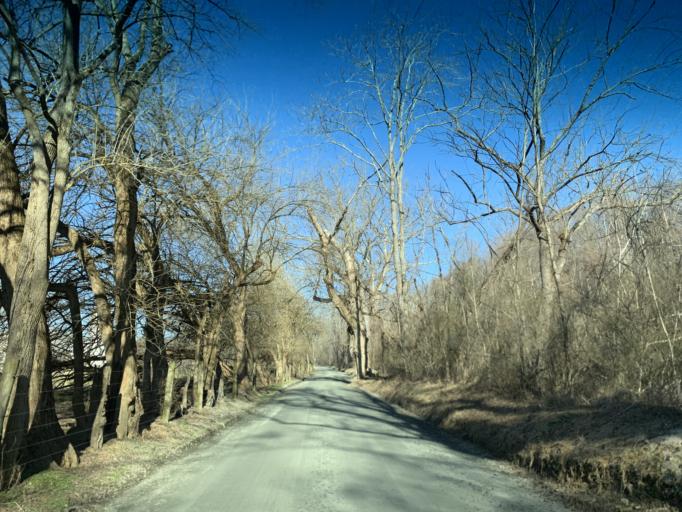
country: US
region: Maryland
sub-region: Harford County
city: Bel Air North
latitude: 39.6170
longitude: -76.3272
